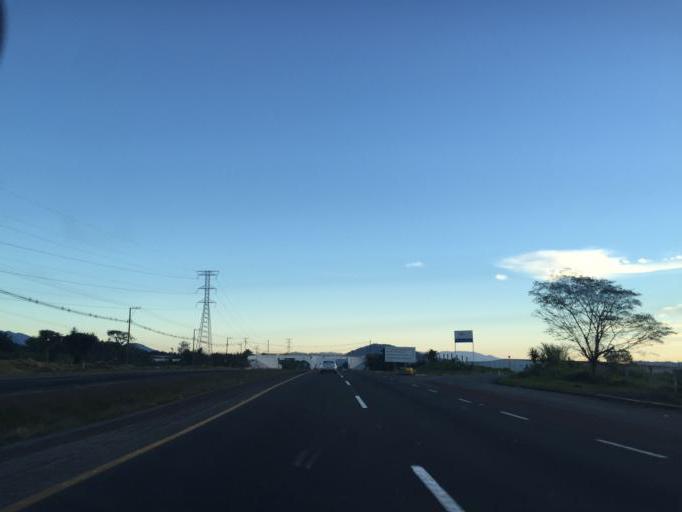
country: MX
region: Veracruz
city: Jalapilla
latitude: 18.8405
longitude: -97.0786
